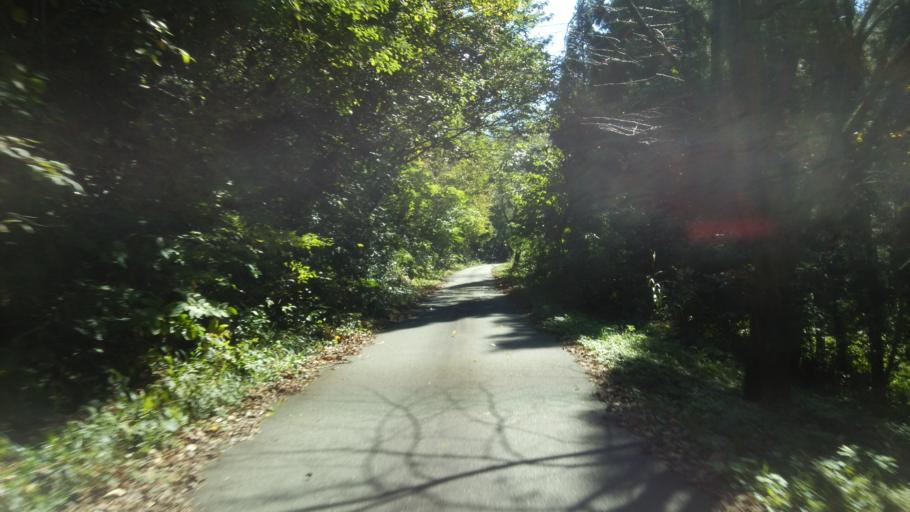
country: JP
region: Fukushima
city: Kitakata
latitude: 37.6216
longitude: 139.9789
